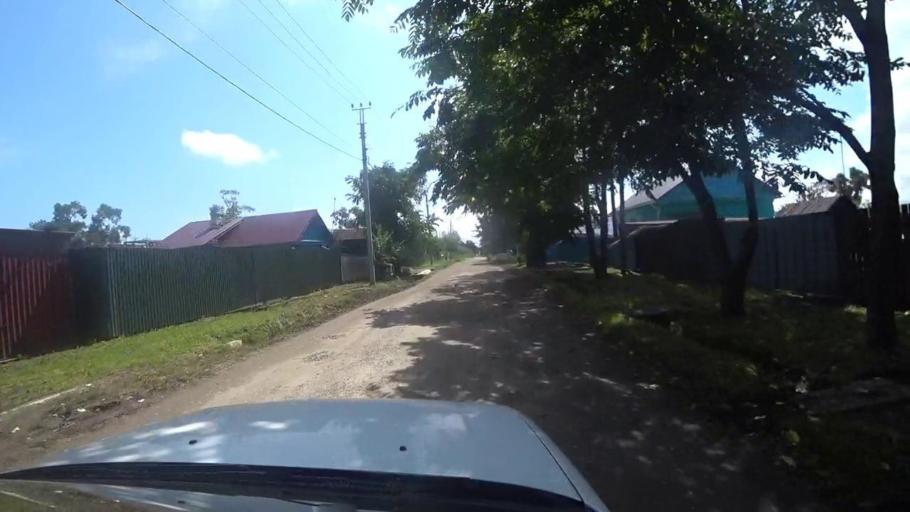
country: RU
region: Primorskiy
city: Dal'nerechensk
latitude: 45.9310
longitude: 133.7391
